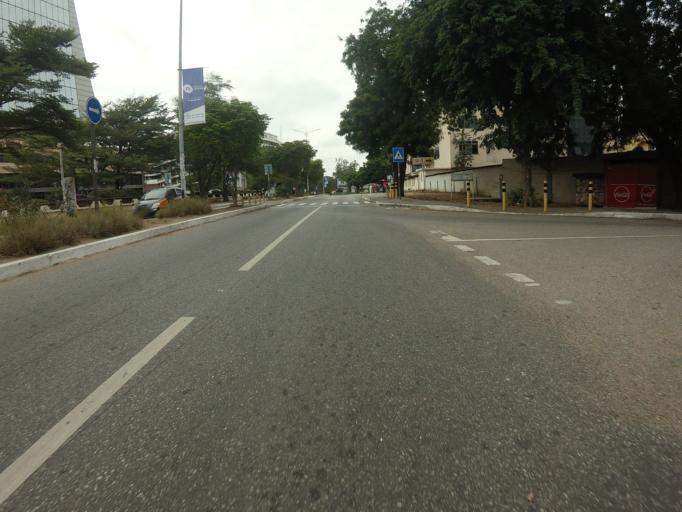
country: GH
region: Greater Accra
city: Accra
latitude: 5.5519
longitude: -0.1988
